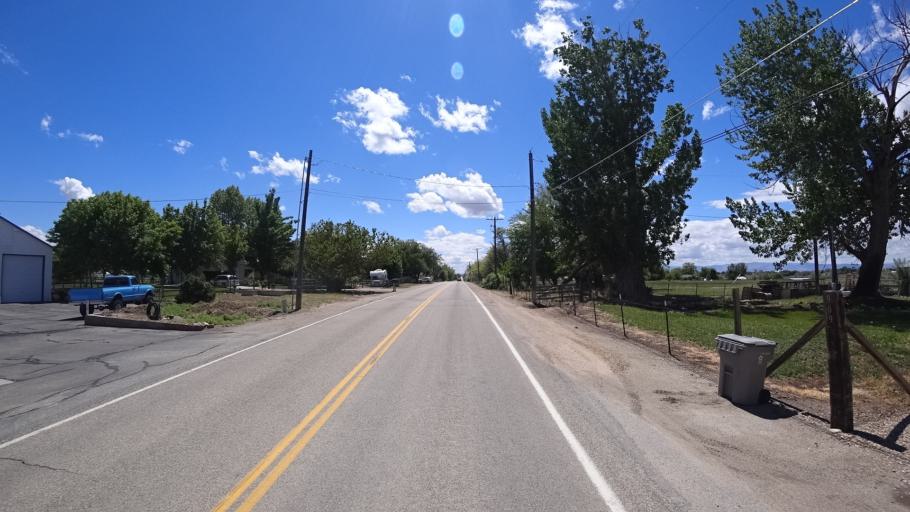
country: US
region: Idaho
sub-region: Ada County
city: Meridian
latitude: 43.5924
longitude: -116.4735
